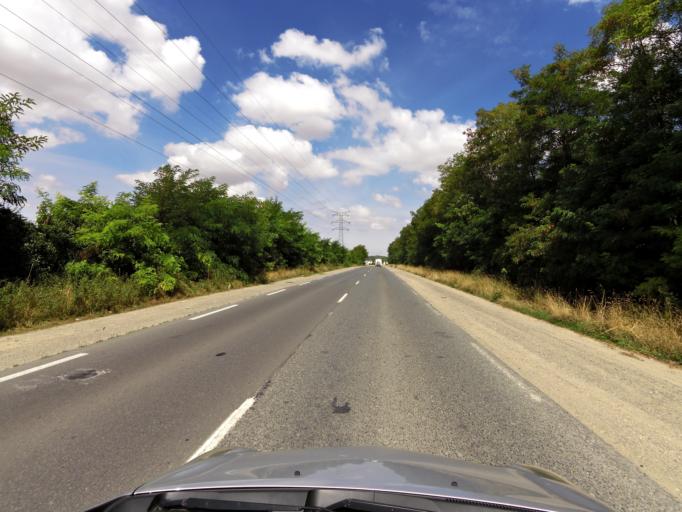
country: FR
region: Ile-de-France
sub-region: Departement de Seine-et-Marne
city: Chauconin-Neufmontiers
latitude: 48.9659
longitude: 2.8595
